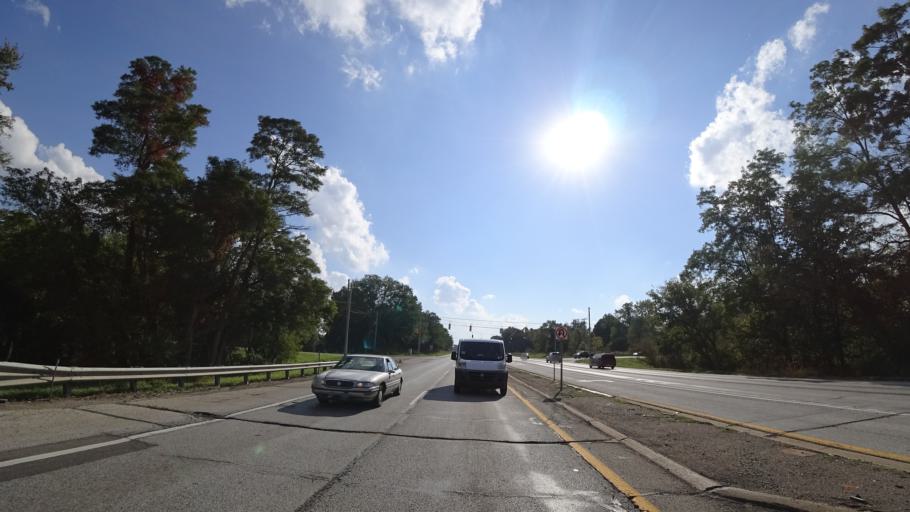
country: US
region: Michigan
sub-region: Saint Joseph County
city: Three Rivers
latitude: 41.9547
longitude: -85.6462
